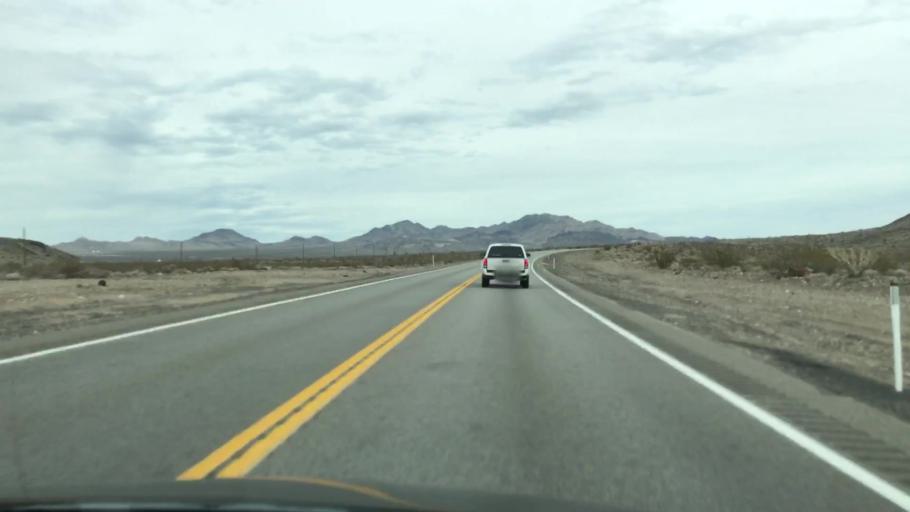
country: US
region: Nevada
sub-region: Nye County
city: Pahrump
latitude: 36.5860
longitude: -116.0584
